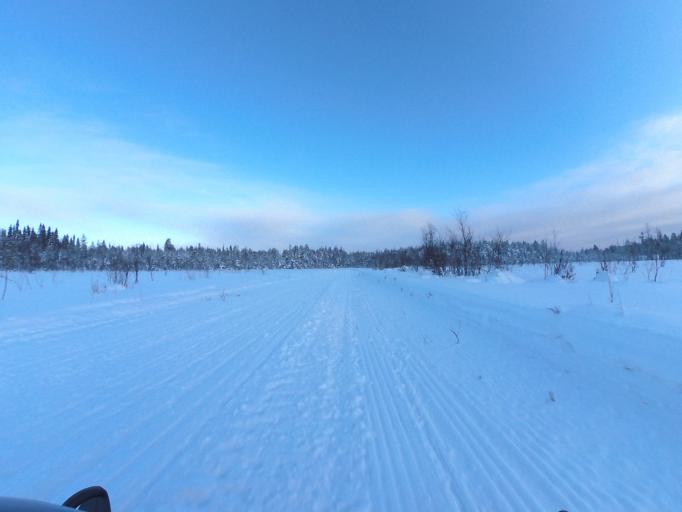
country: FI
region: Lapland
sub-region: Rovaniemi
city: Rovaniemi
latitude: 66.5157
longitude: 25.9961
